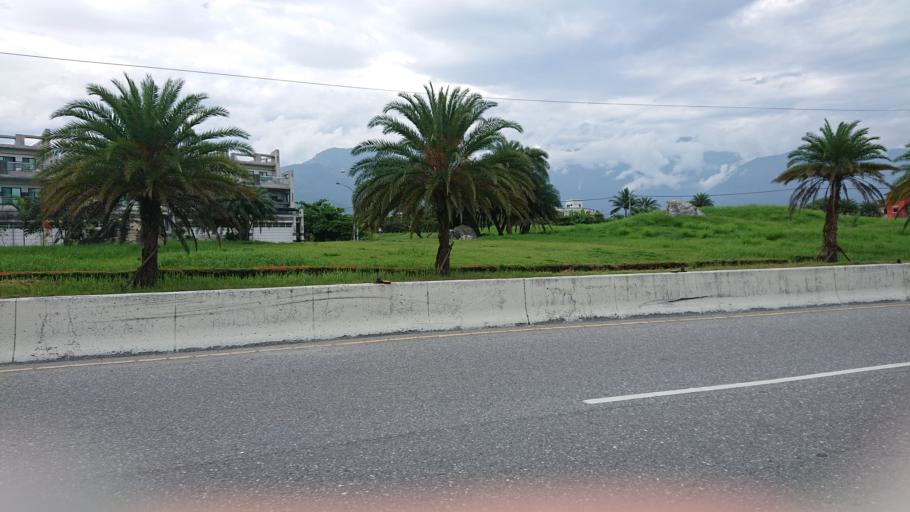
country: TW
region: Taiwan
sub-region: Hualien
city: Hualian
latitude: 23.9400
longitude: 121.5944
